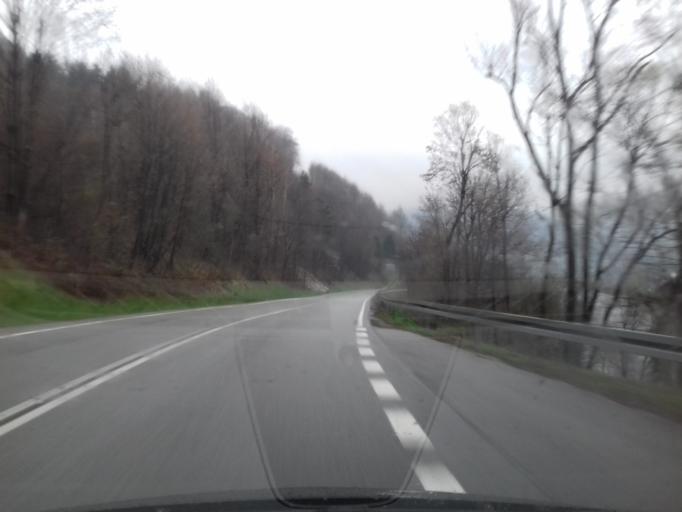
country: PL
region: Lesser Poland Voivodeship
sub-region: Powiat nowosadecki
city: Piwniczna-Zdroj
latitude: 49.4584
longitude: 20.6939
